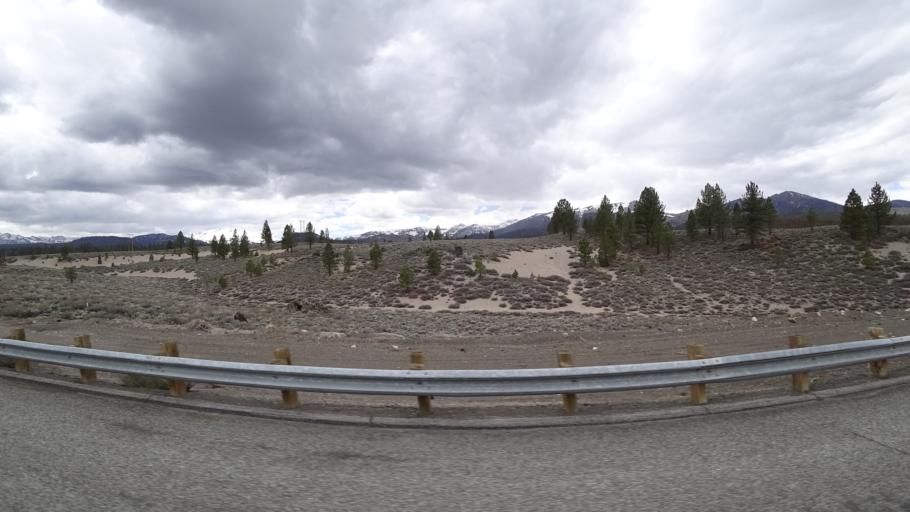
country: US
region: California
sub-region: Mono County
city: Mammoth Lakes
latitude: 37.7419
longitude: -118.9759
